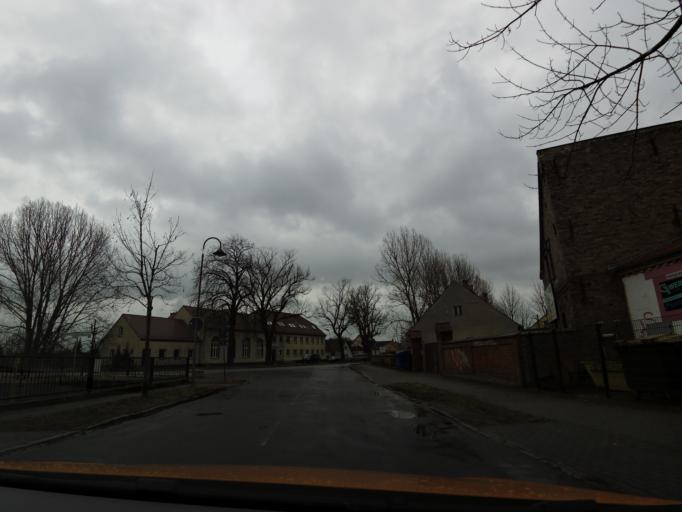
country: DE
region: Brandenburg
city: Rangsdorf
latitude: 52.3234
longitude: 13.4372
